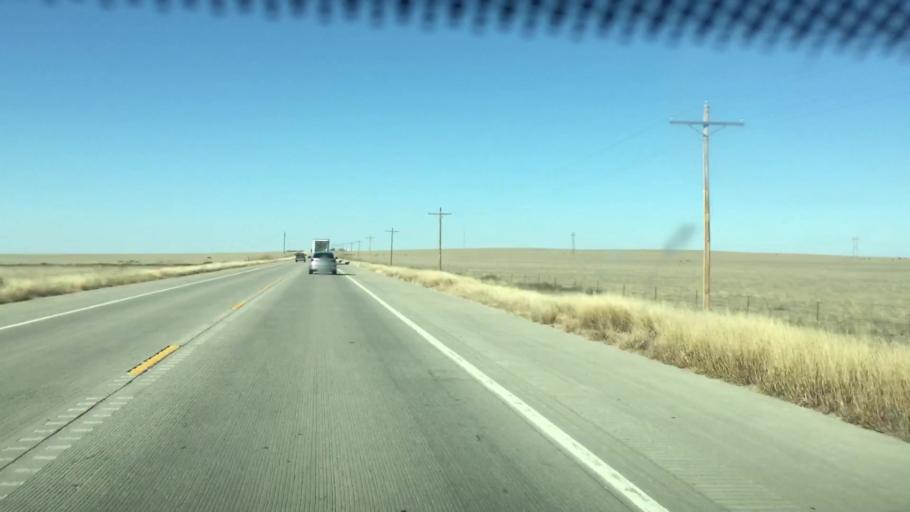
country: US
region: Colorado
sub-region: Prowers County
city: Lamar
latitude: 38.2576
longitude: -102.7239
